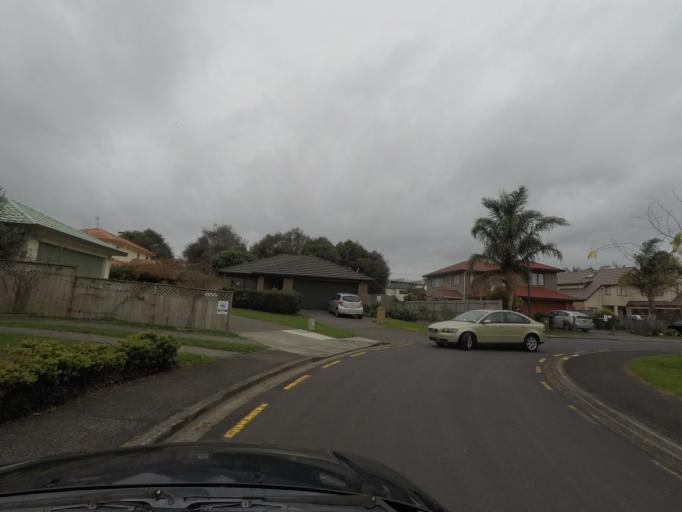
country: NZ
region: Auckland
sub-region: Auckland
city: Rosebank
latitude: -36.8965
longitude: 174.6877
